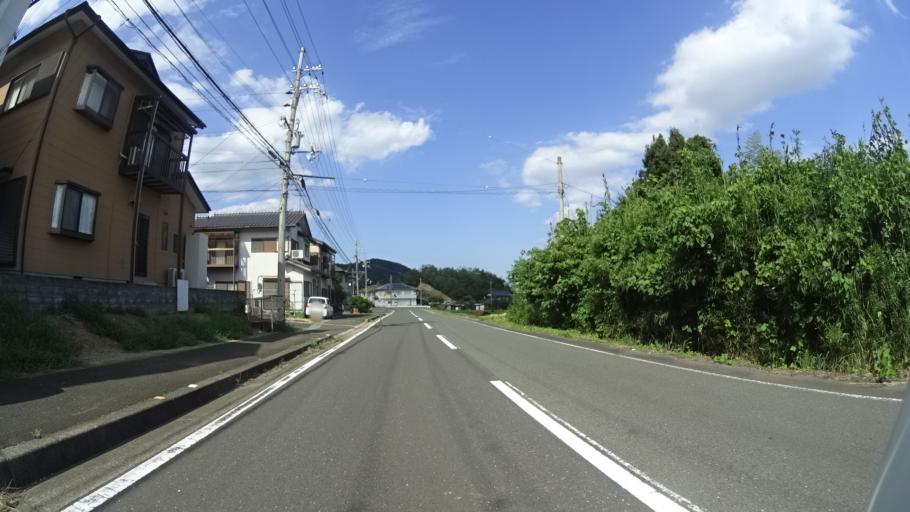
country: JP
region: Kyoto
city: Maizuru
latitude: 35.4541
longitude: 135.3056
